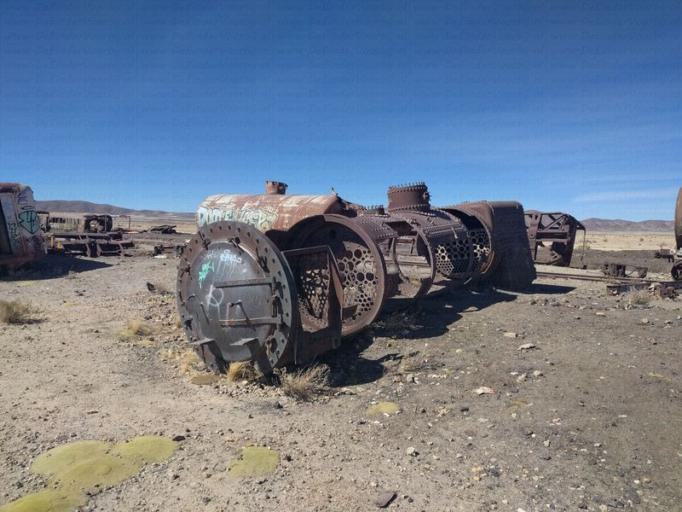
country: BO
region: Potosi
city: Uyuni
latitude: -20.4793
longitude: -66.8352
